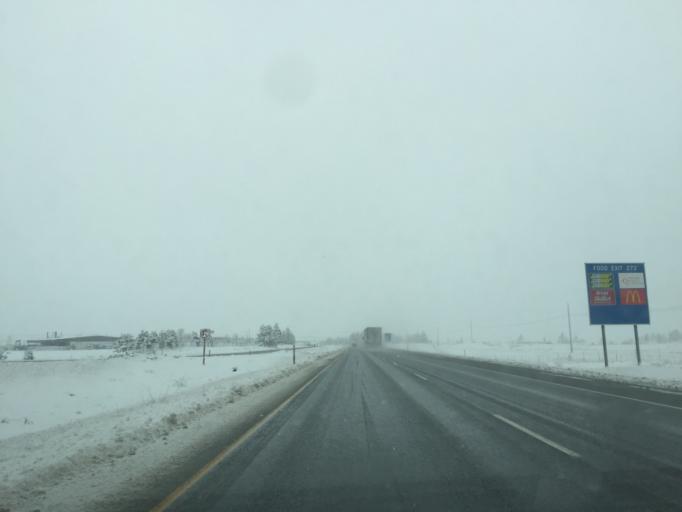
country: US
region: Washington
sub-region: Spokane County
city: Airway Heights
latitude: 47.5979
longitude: -117.5535
